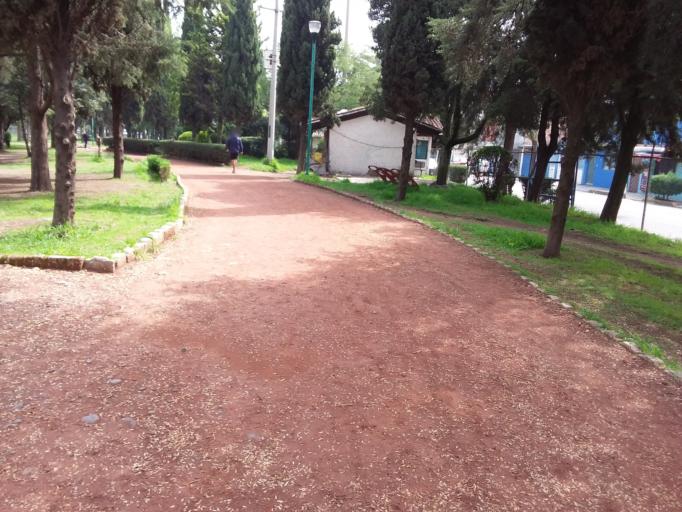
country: MX
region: Mexico
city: Toluca
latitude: 19.3156
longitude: -99.6492
